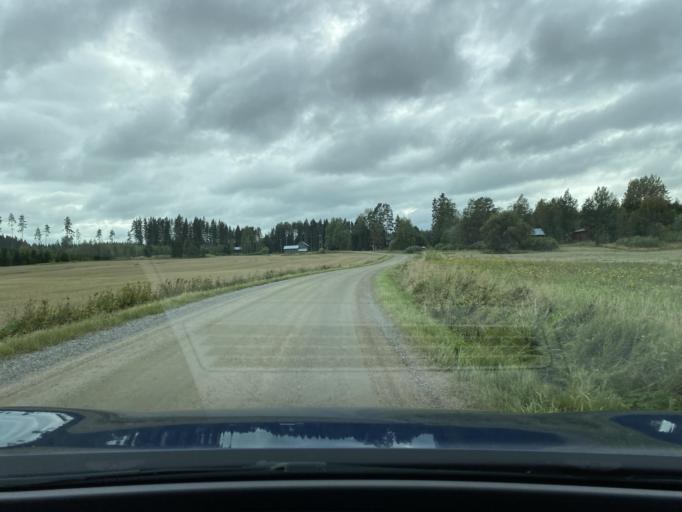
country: FI
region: Pirkanmaa
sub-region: Lounais-Pirkanmaa
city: Punkalaidun
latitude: 61.1821
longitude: 23.1843
